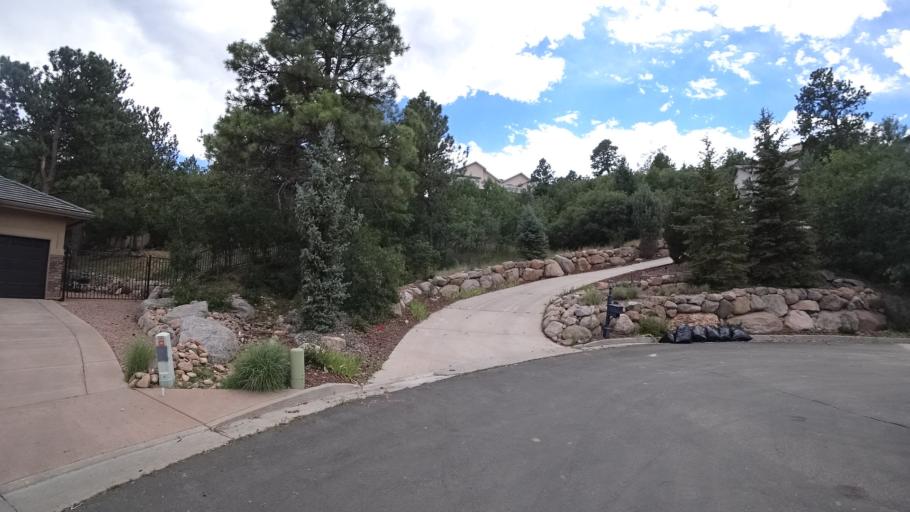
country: US
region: Colorado
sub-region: El Paso County
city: Fort Carson
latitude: 38.7666
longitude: -104.8334
